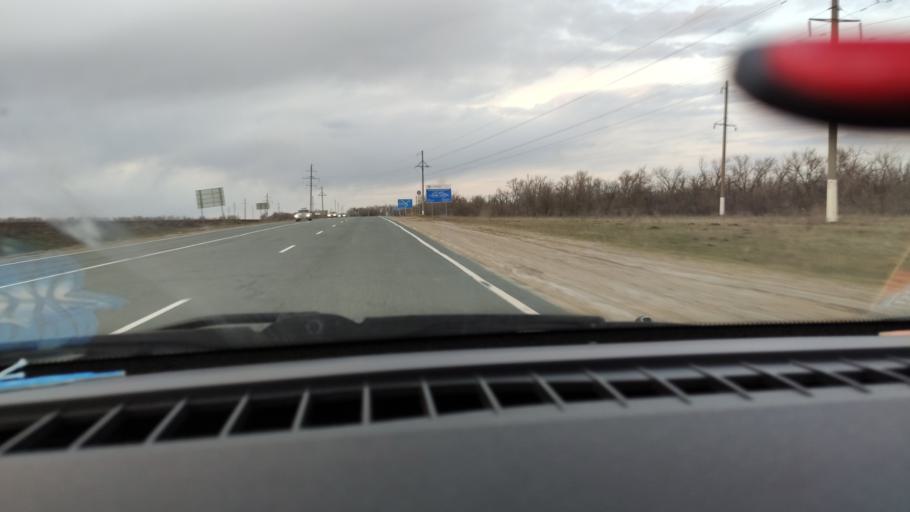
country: RU
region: Saratov
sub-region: Saratovskiy Rayon
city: Saratov
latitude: 51.7729
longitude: 46.0863
